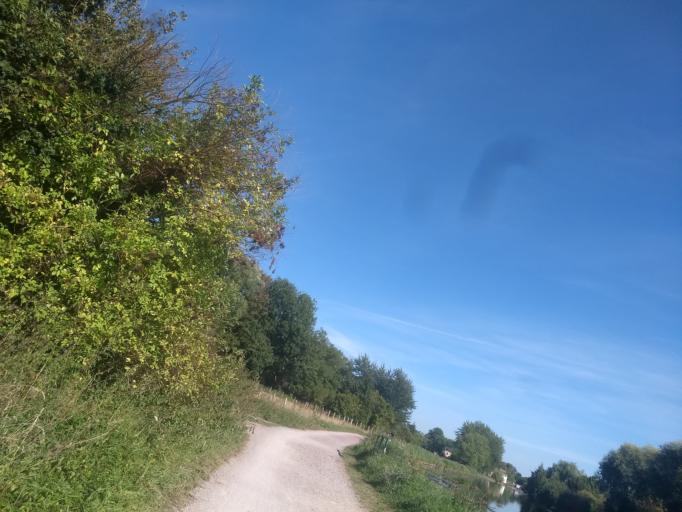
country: FR
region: Nord-Pas-de-Calais
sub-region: Departement du Pas-de-Calais
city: Feuchy
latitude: 50.3000
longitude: 2.8315
